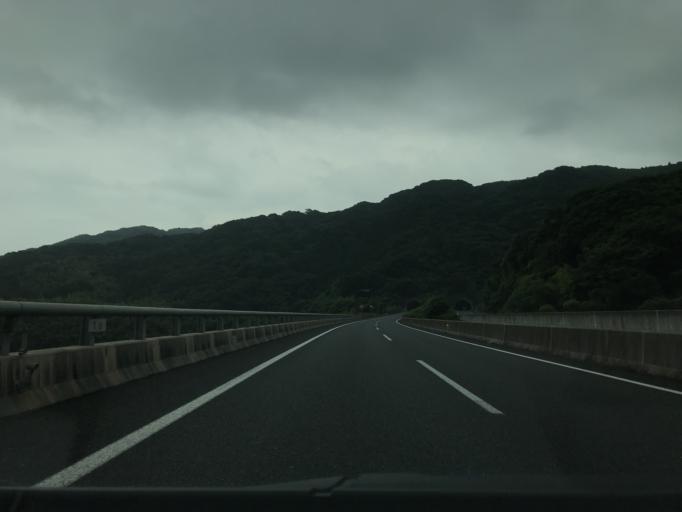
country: JP
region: Fukuoka
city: Kitakyushu
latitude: 33.8149
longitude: 130.9036
